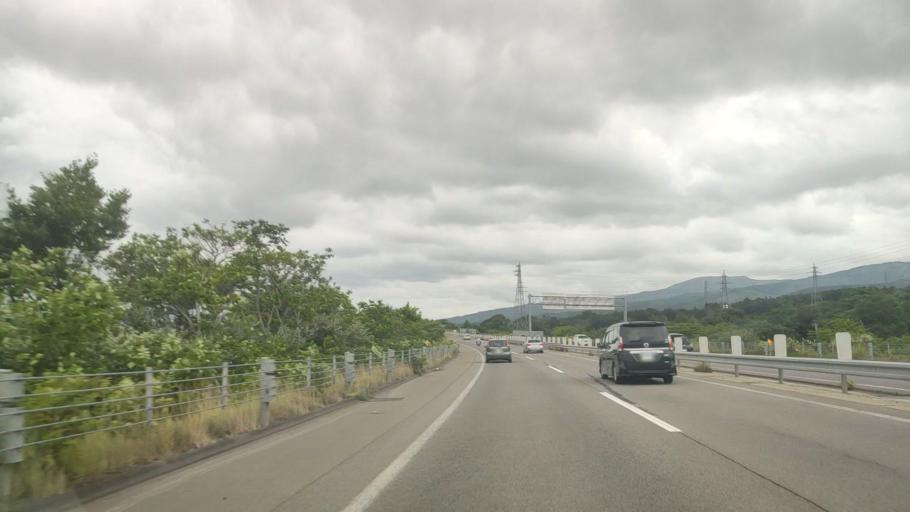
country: JP
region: Hokkaido
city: Nanae
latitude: 41.8557
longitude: 140.7376
